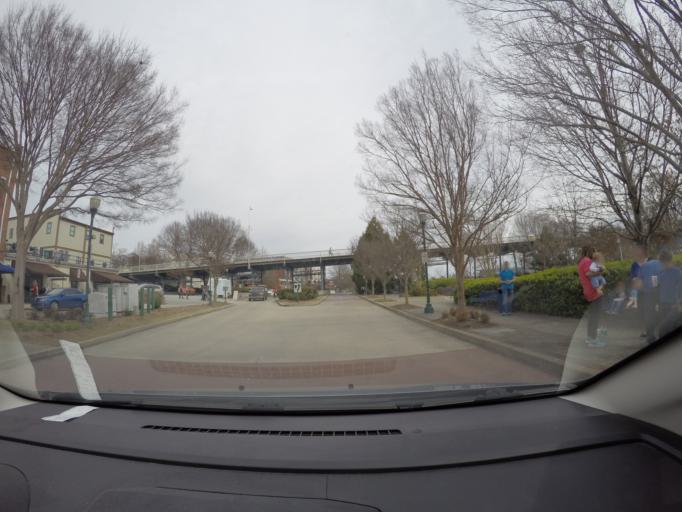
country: US
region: Tennessee
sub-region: Hamilton County
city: Chattanooga
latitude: 35.0619
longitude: -85.3073
